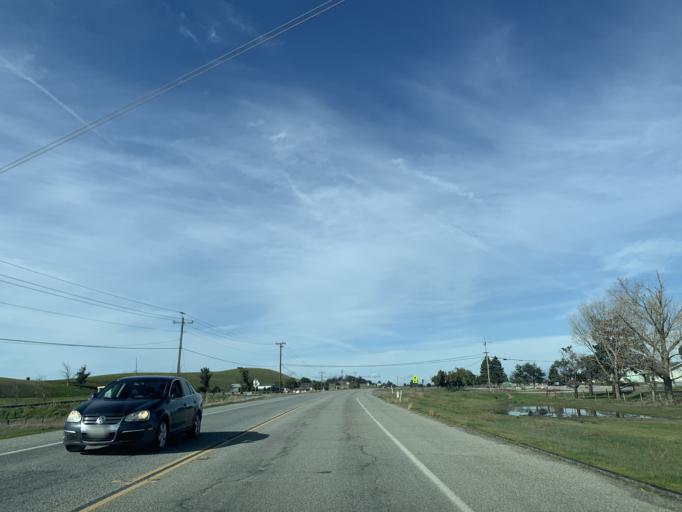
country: US
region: California
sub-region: San Benito County
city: Ridgemark
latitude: 36.7994
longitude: -121.3351
